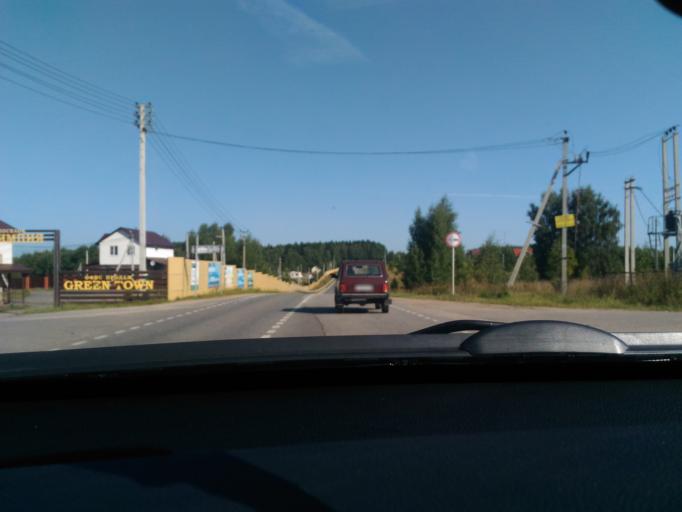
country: RU
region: Moskovskaya
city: Dedenevo
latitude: 56.2419
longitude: 37.5476
